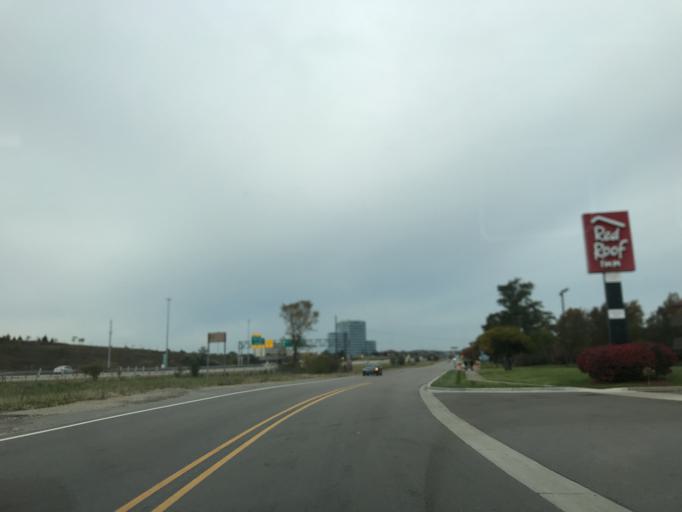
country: US
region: Michigan
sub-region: Oakland County
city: Bingham Farms
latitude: 42.4937
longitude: -83.2884
